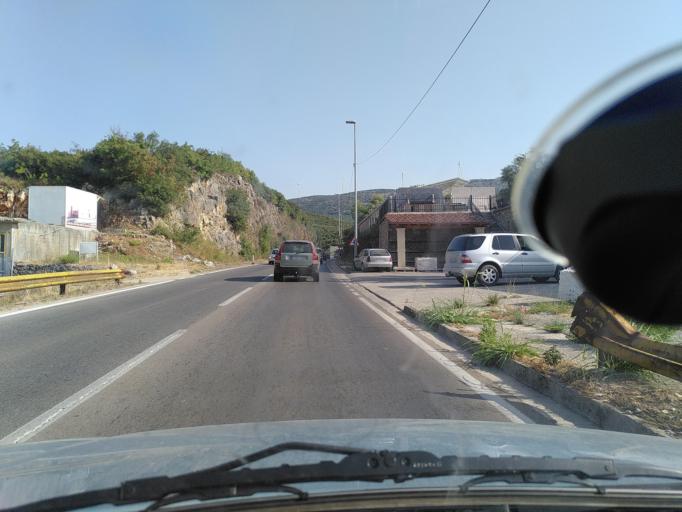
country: ME
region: Ulcinj
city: Ulcinj
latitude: 41.9567
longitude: 19.1909
